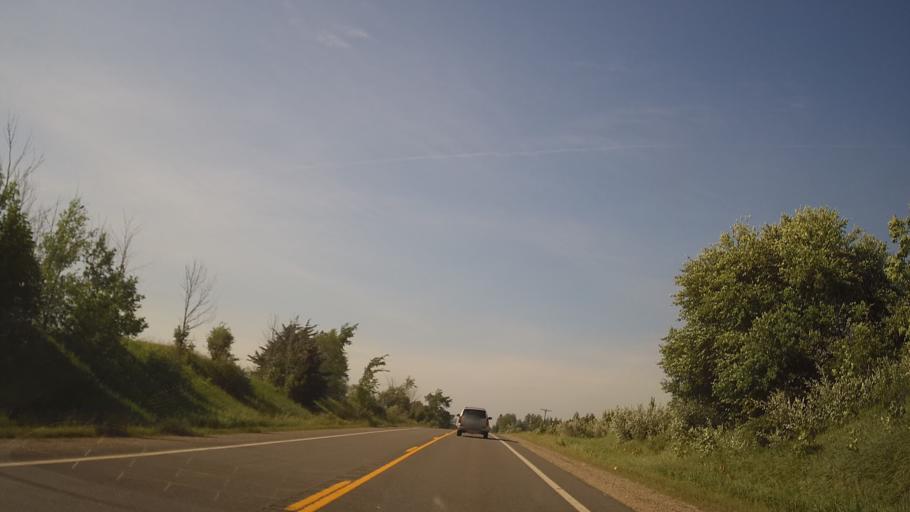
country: US
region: Michigan
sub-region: Ogemaw County
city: West Branch
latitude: 44.3838
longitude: -84.1161
